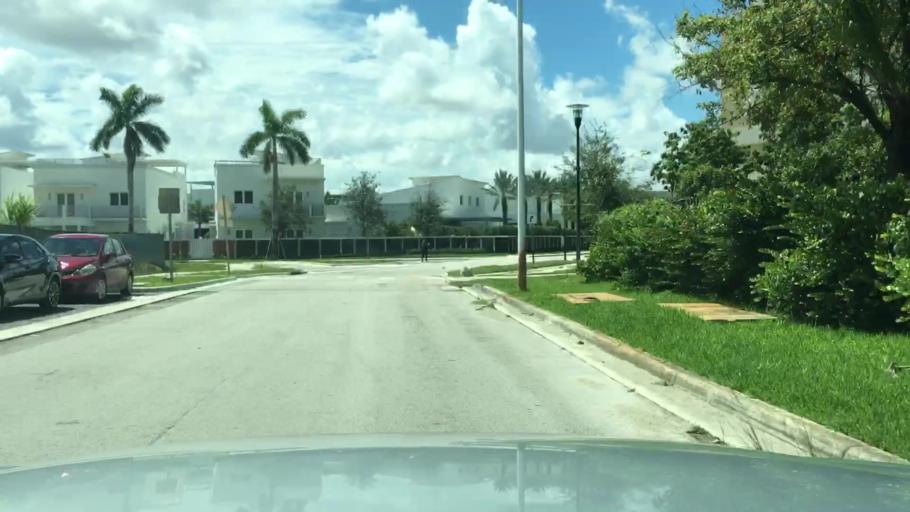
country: US
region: Florida
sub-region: Miami-Dade County
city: Doral
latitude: 25.8073
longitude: -80.3332
